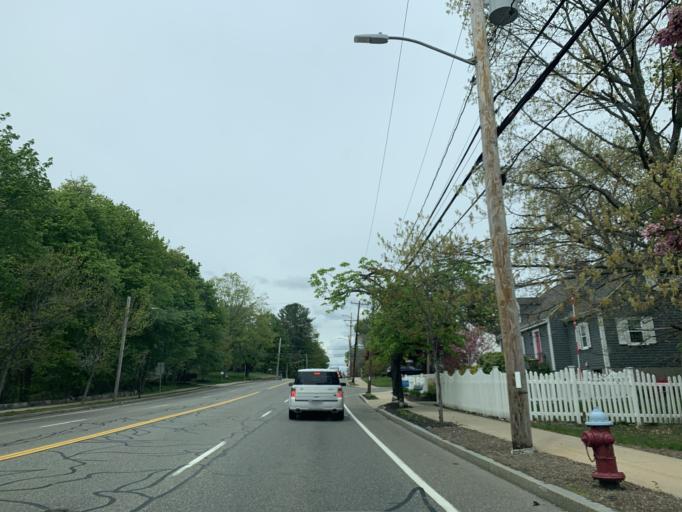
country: US
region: Massachusetts
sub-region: Norfolk County
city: Milton
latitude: 42.2533
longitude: -71.0762
